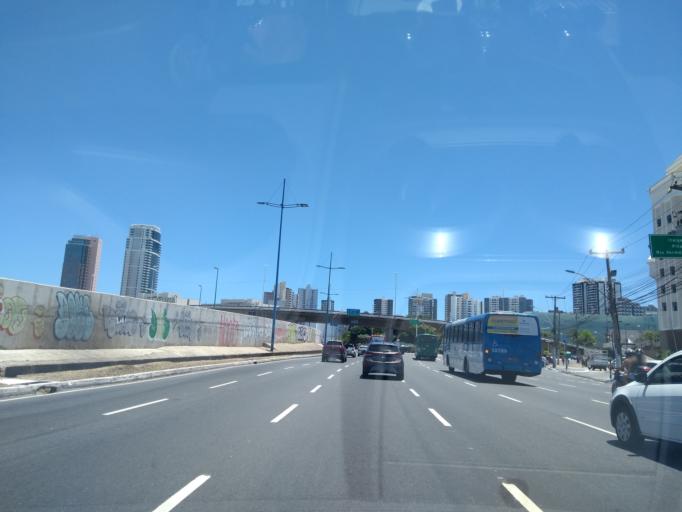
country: BR
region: Bahia
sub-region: Salvador
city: Salvador
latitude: -12.9797
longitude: -38.4678
